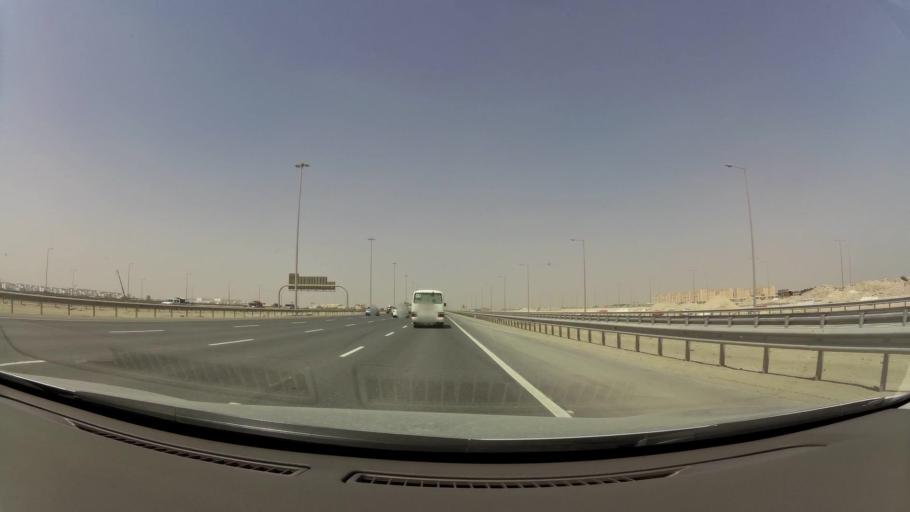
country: QA
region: Baladiyat Umm Salal
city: Umm Salal Muhammad
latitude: 25.4142
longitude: 51.4232
